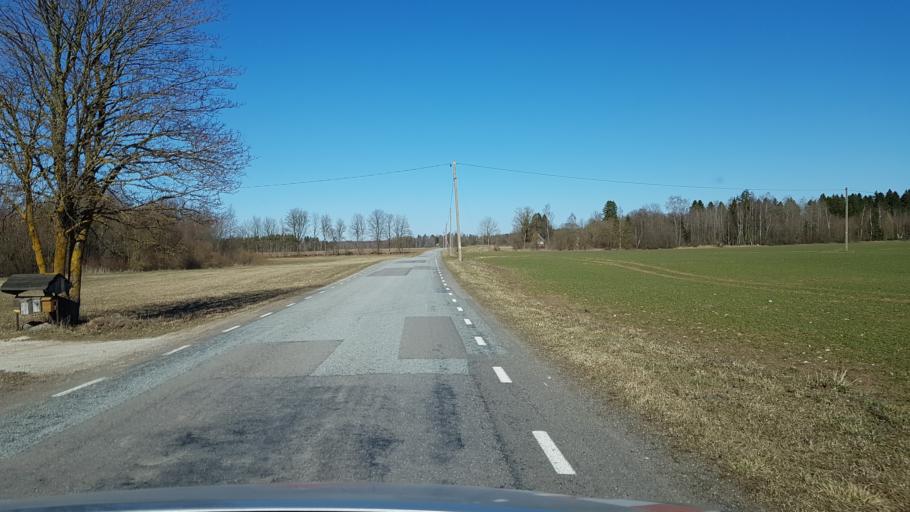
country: EE
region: Laeaene-Virumaa
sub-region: Someru vald
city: Someru
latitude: 59.3759
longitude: 26.4545
